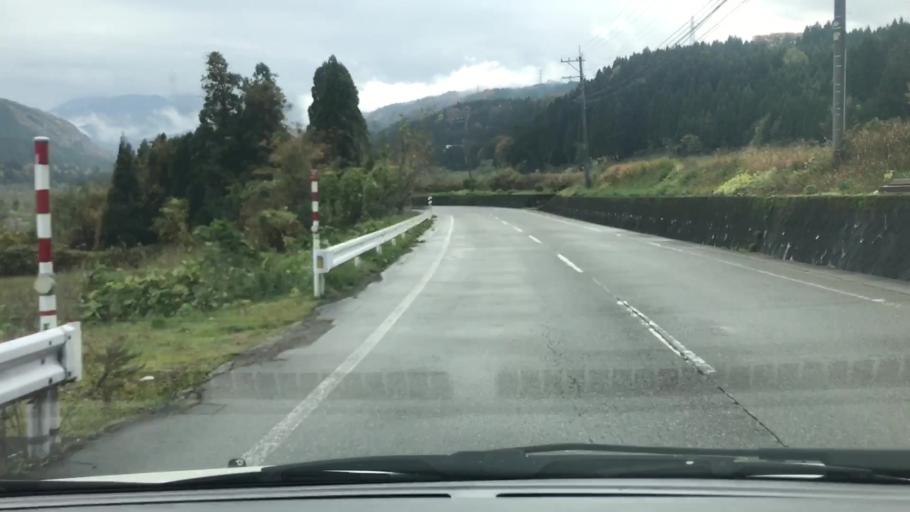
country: JP
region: Toyama
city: Kamiichi
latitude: 36.5898
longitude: 137.3184
